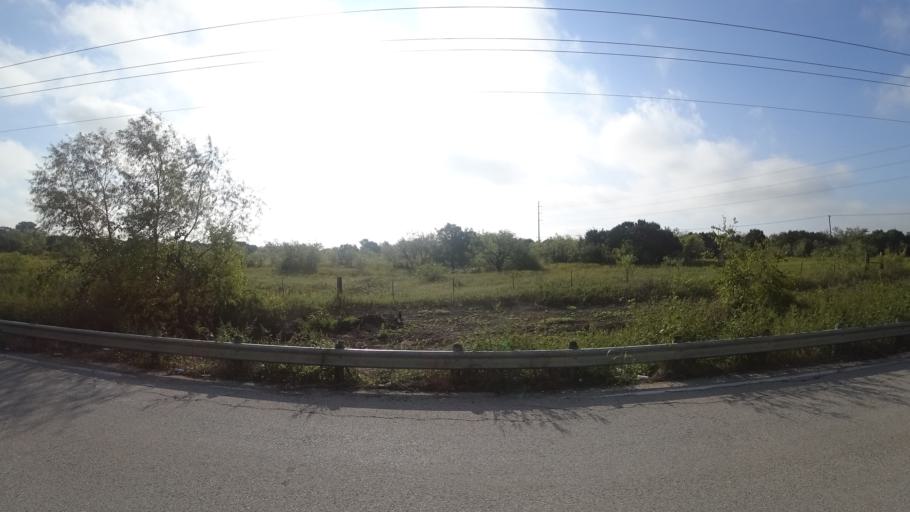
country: US
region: Texas
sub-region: Travis County
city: Manor
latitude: 30.3538
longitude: -97.6377
